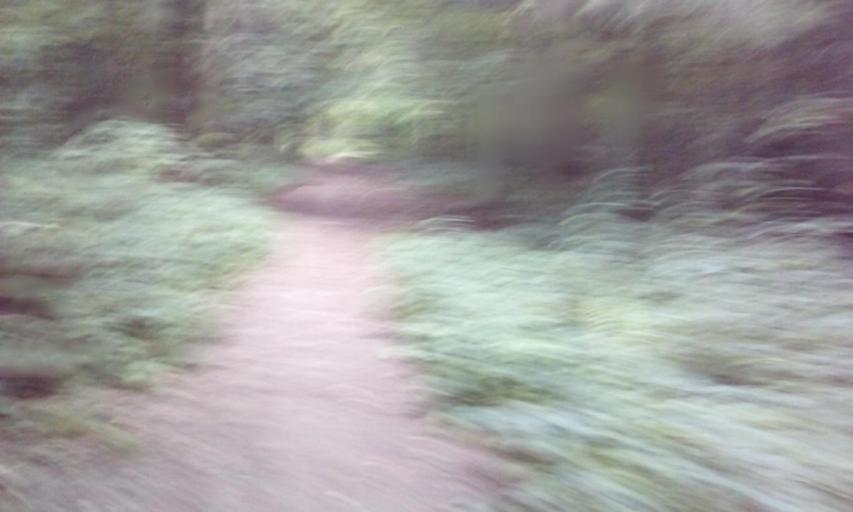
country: RU
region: Moskovskaya
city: Moskovskiy
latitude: 55.5964
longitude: 37.3330
